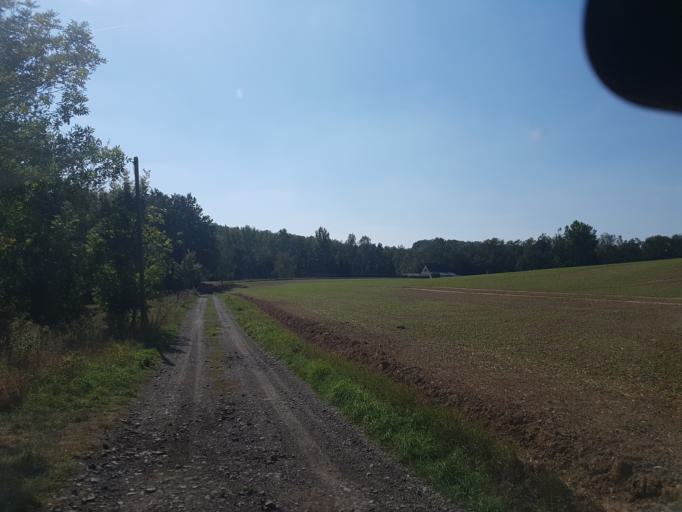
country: DE
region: Saxony
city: Kriebstein
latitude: 51.0530
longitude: 13.0006
